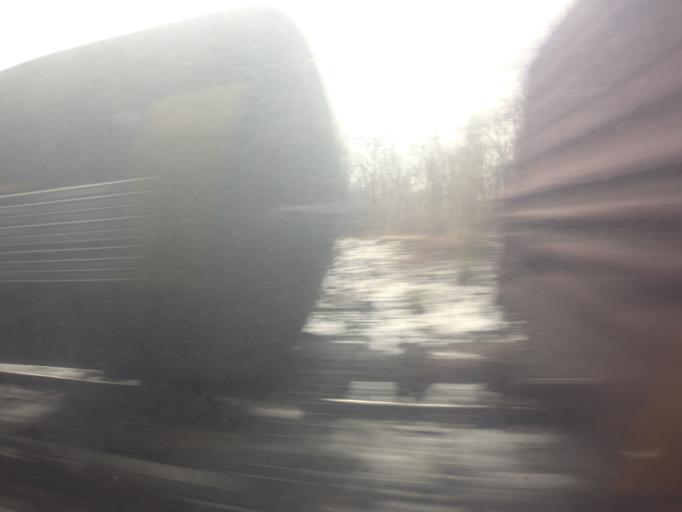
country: CA
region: Ontario
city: Quinte West
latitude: 44.0164
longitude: -77.8100
